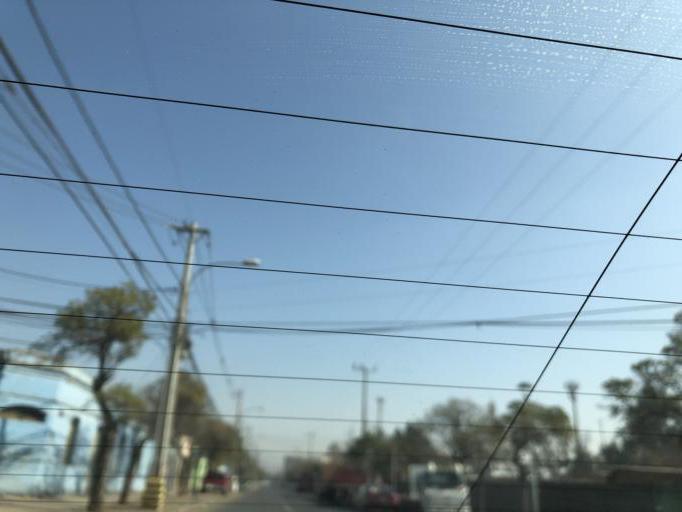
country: CL
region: Santiago Metropolitan
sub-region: Provincia de Cordillera
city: Puente Alto
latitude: -33.6069
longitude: -70.5677
